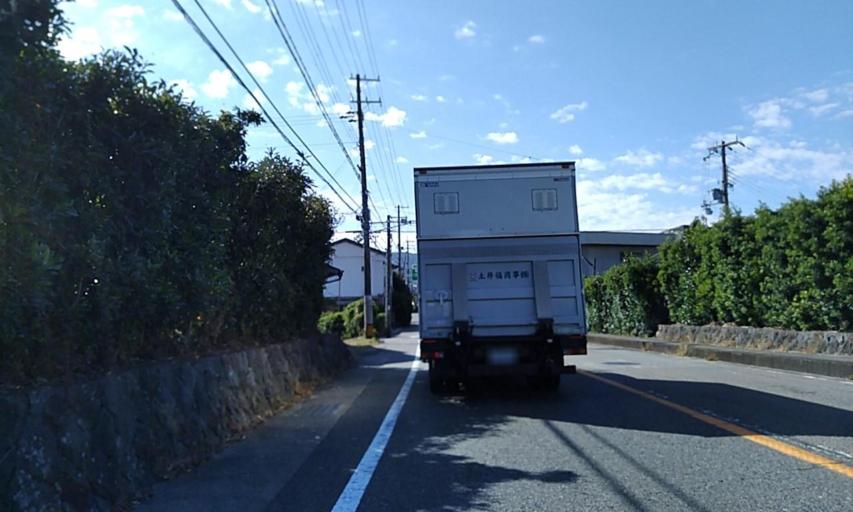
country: JP
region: Wakayama
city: Kainan
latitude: 34.0322
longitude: 135.1852
